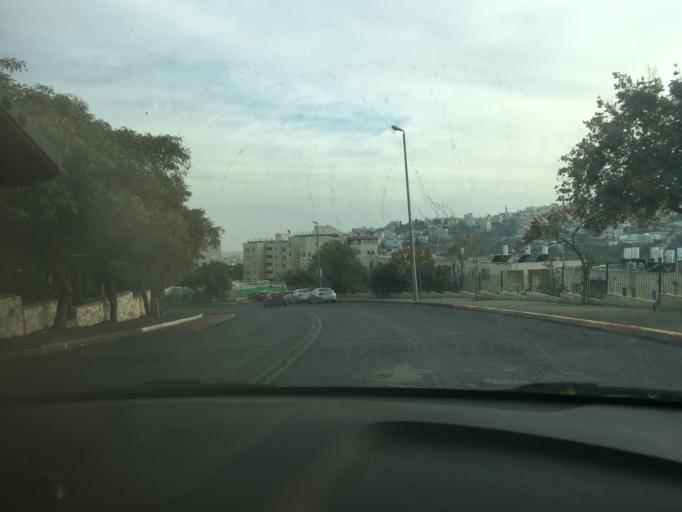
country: IL
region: Jerusalem
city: Jerusalem
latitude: 31.7468
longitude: 35.2313
